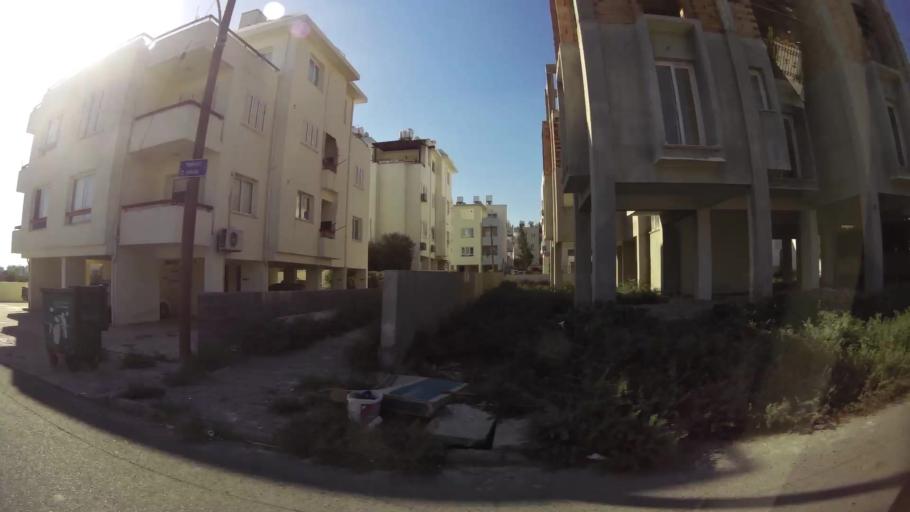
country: CY
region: Lefkosia
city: Nicosia
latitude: 35.2139
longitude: 33.3146
